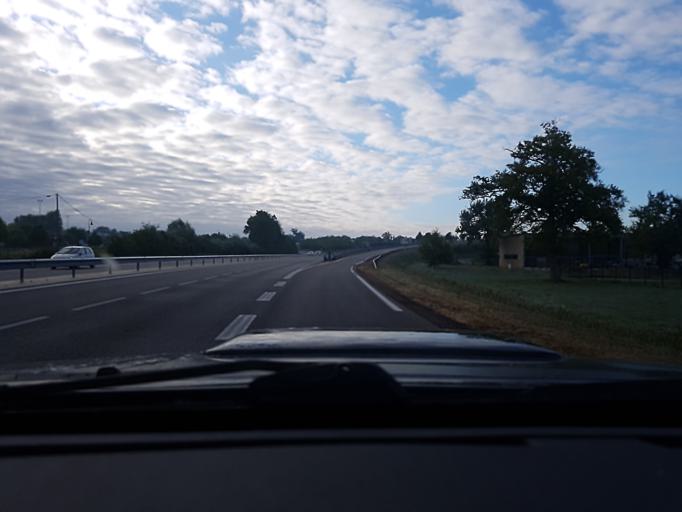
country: FR
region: Pays de la Loire
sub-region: Departement de la Vendee
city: Aizenay
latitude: 46.7491
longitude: -1.6260
